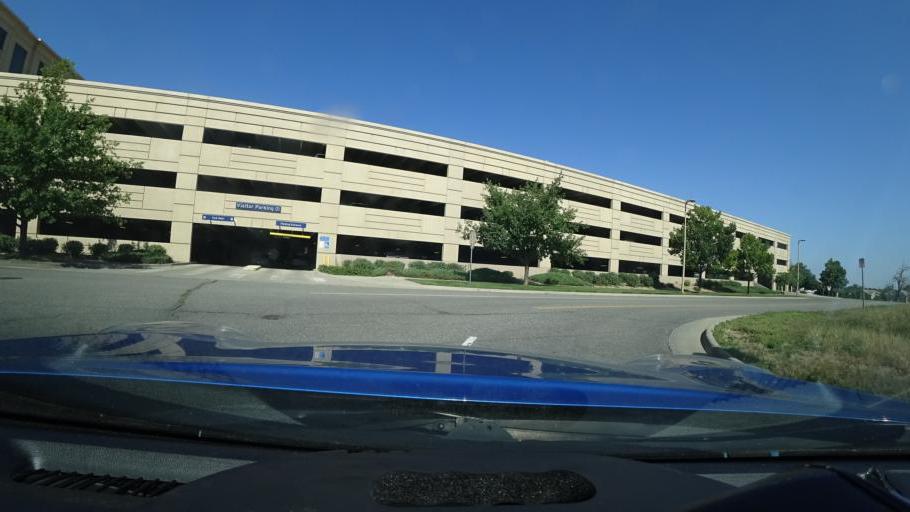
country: US
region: Colorado
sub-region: Adams County
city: Aurora
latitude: 39.7116
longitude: -104.8118
